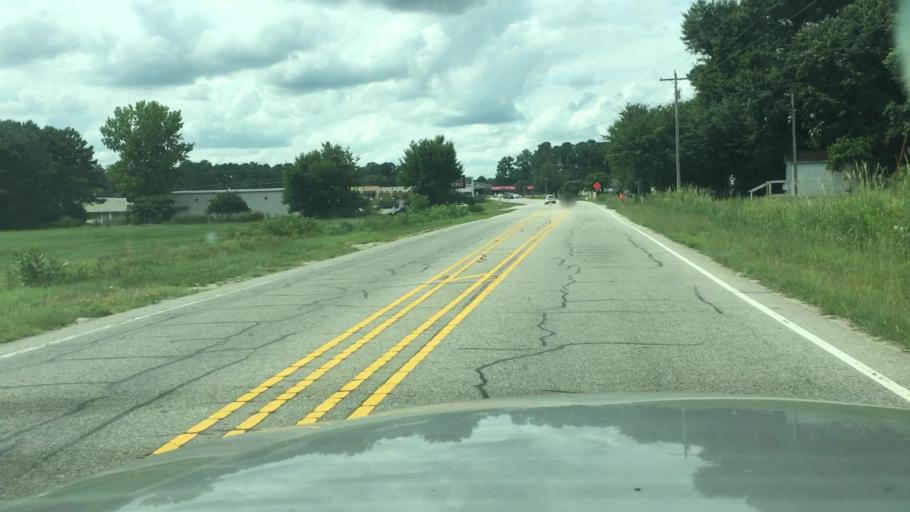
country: US
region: North Carolina
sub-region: Hoke County
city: Rockfish
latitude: 35.0134
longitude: -79.0054
